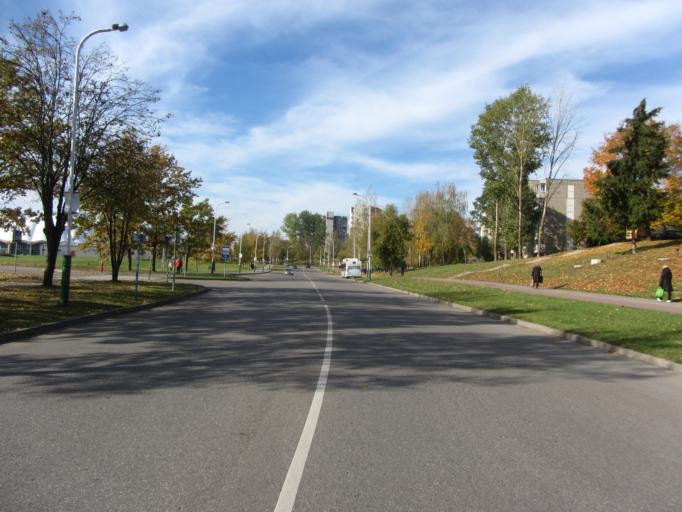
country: LT
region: Vilnius County
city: Elektrenai
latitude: 54.7857
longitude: 24.6748
